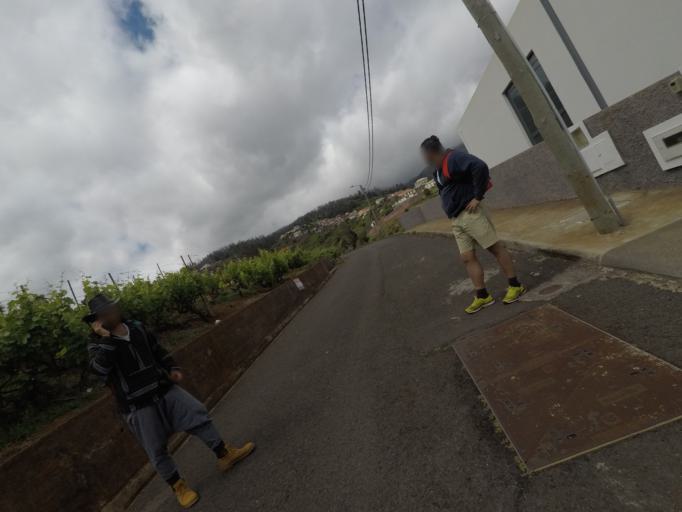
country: PT
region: Madeira
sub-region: Calheta
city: Estreito da Calheta
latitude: 32.7328
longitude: -17.1819
